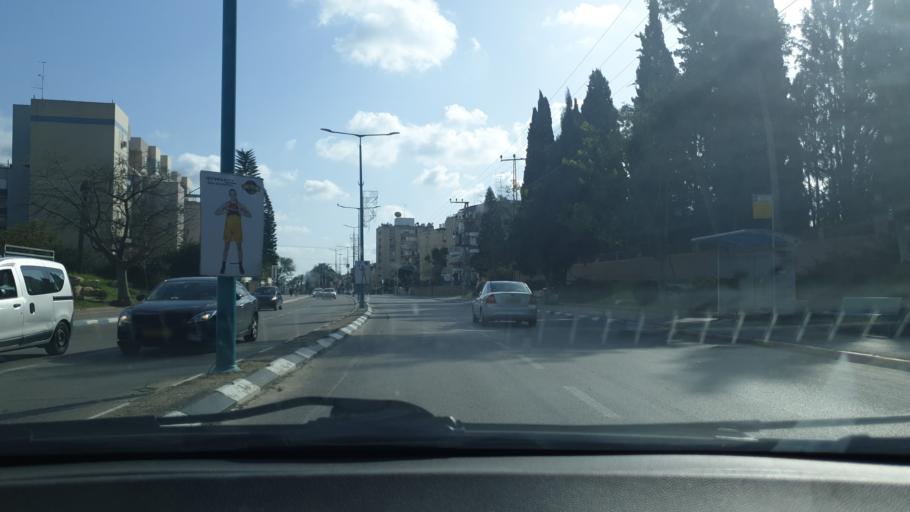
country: IL
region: Central District
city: Ramla
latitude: 31.9278
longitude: 34.8642
